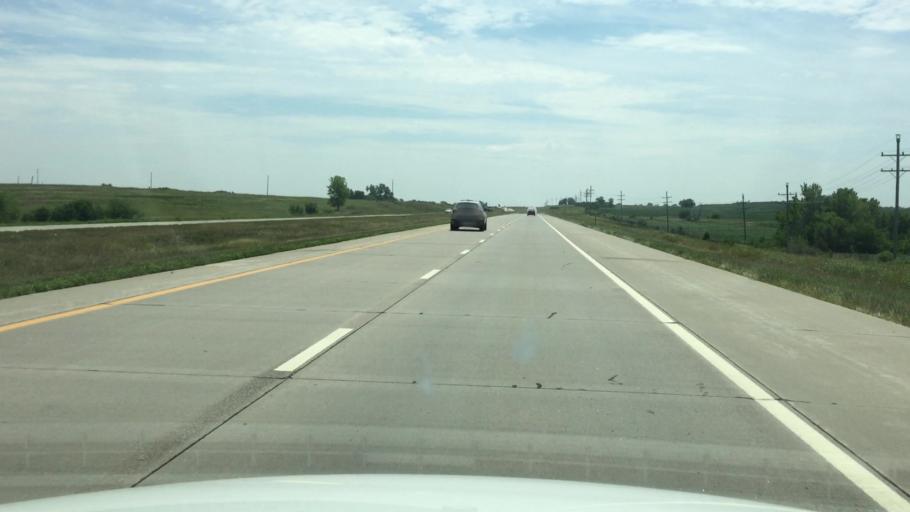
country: US
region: Kansas
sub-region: Shawnee County
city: Silver Lake
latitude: 39.2352
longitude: -95.7196
